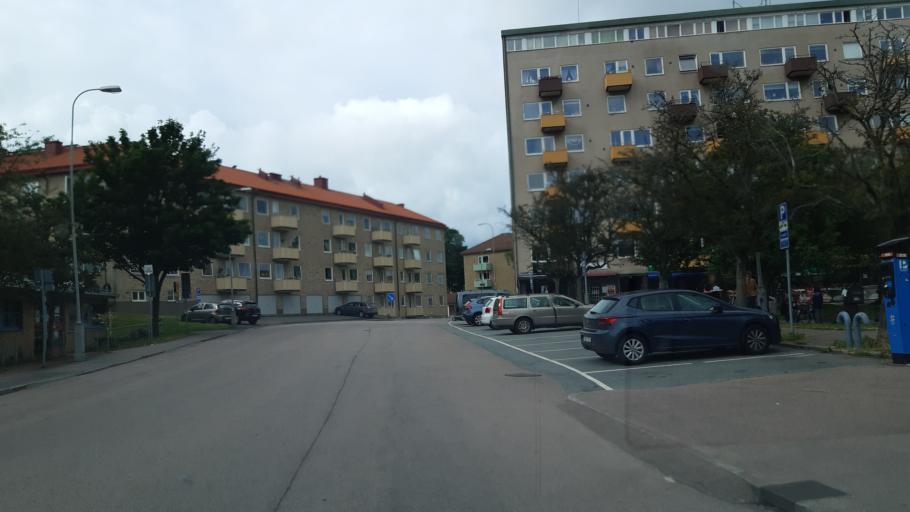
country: SE
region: Vaestra Goetaland
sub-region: Goteborg
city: Eriksbo
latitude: 57.7147
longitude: 12.0470
